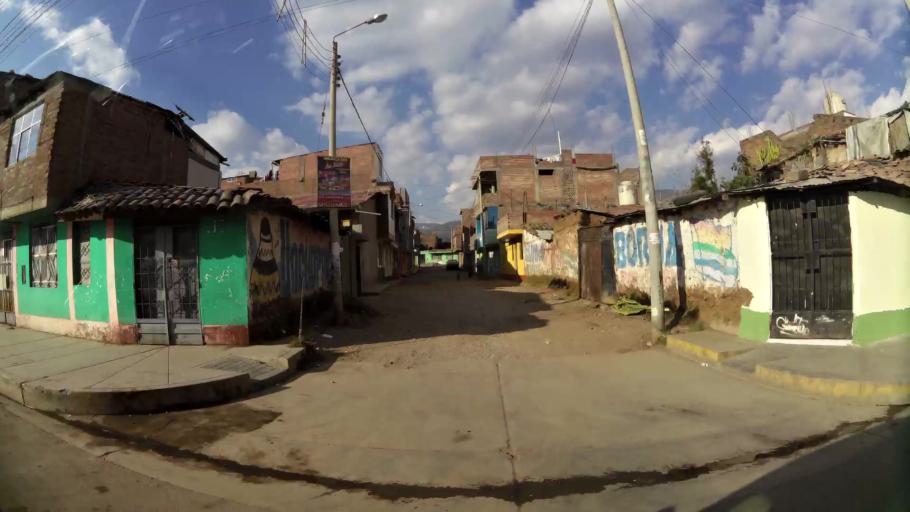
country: PE
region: Junin
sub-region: Provincia de Huancayo
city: El Tambo
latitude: -12.0486
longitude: -75.2159
